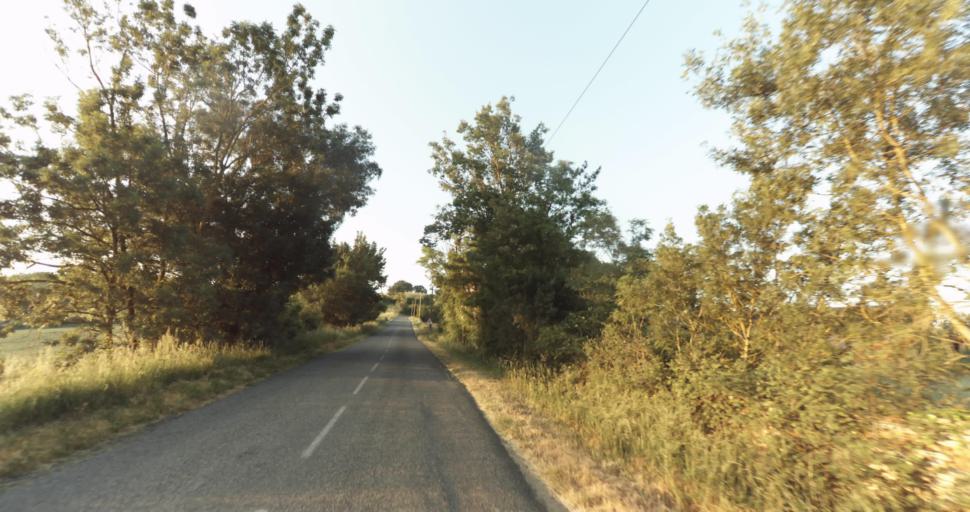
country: FR
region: Midi-Pyrenees
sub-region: Departement du Gers
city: Pujaudran
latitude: 43.6147
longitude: 1.1577
